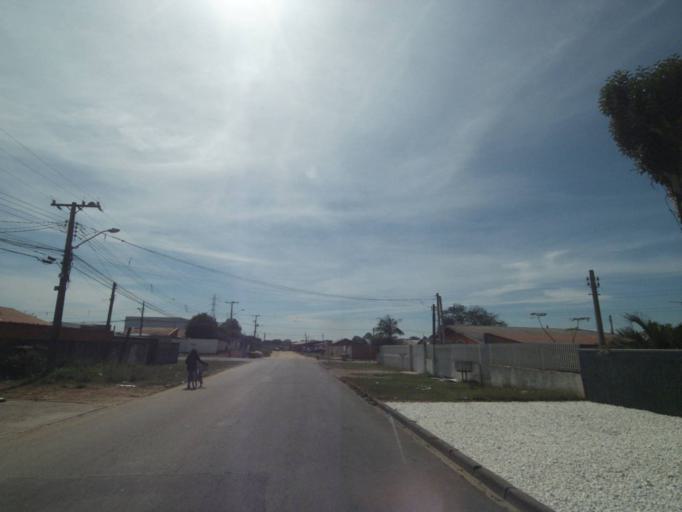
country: BR
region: Parana
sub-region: Sao Jose Dos Pinhais
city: Sao Jose dos Pinhais
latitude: -25.5109
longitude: -49.2179
